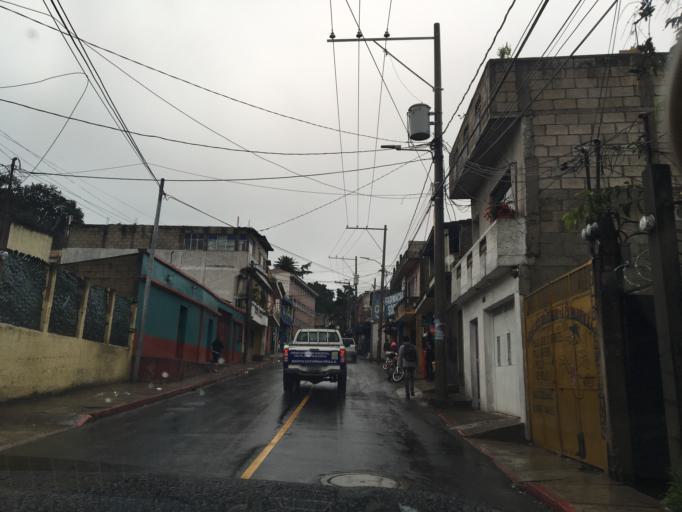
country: GT
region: Guatemala
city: Santa Catarina Pinula
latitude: 14.5628
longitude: -90.4895
